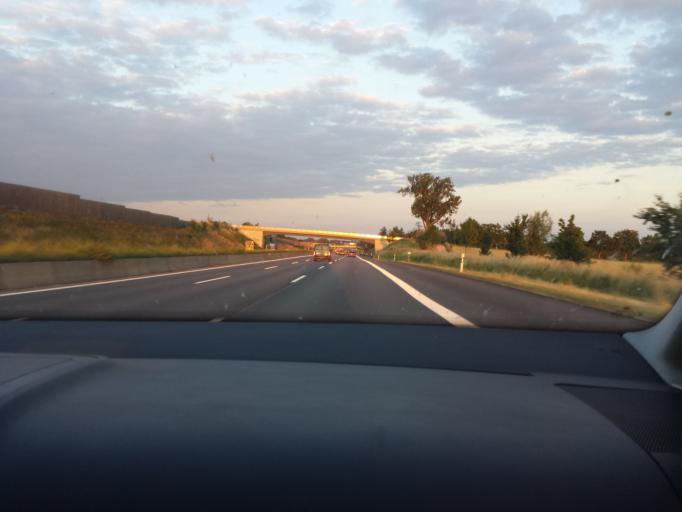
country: DE
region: Bavaria
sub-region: Upper Bavaria
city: Maisach
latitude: 48.2550
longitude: 11.3052
